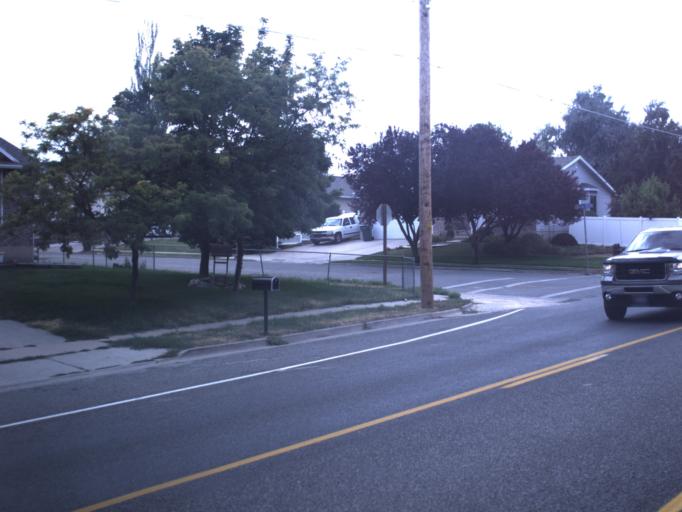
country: US
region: Utah
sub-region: Weber County
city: West Haven
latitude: 41.1738
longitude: -112.0645
